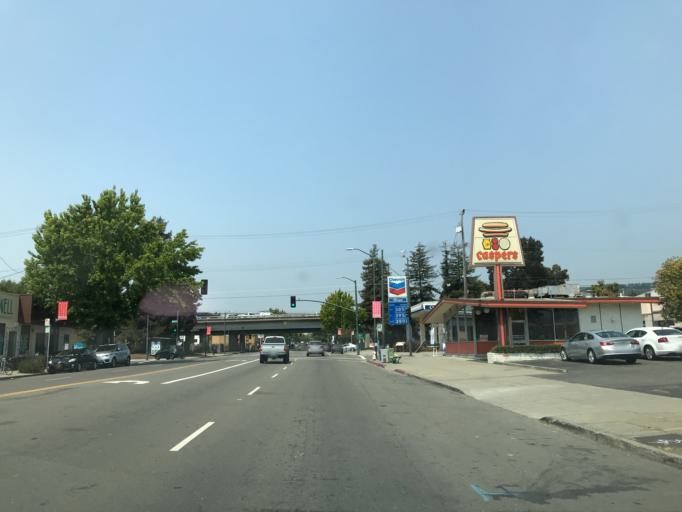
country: US
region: California
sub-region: Alameda County
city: Emeryville
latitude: 37.8396
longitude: -122.2619
